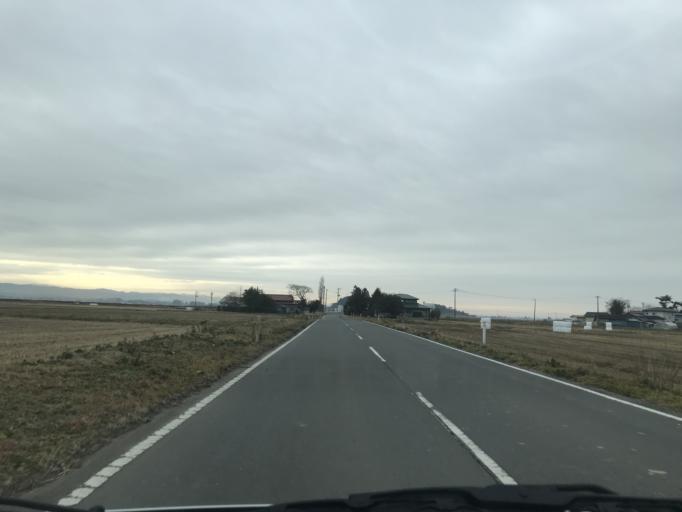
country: JP
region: Iwate
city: Ichinoseki
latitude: 38.7411
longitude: 141.2259
